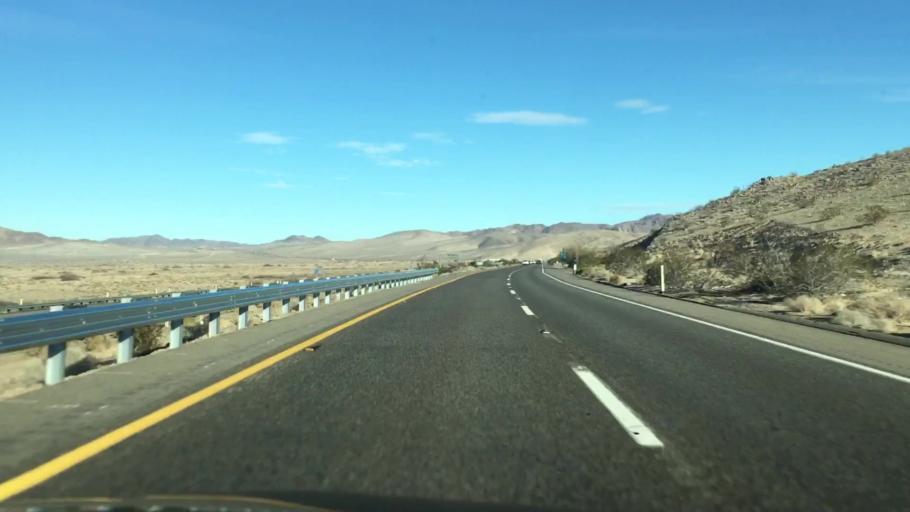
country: US
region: California
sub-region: San Bernardino County
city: Fort Irwin
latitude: 35.0981
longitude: -116.2912
